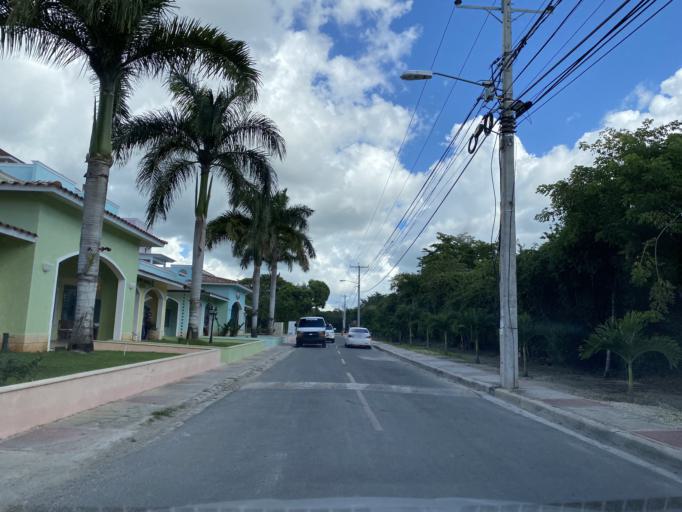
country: DO
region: La Romana
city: La Romana
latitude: 18.3500
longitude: -68.8235
